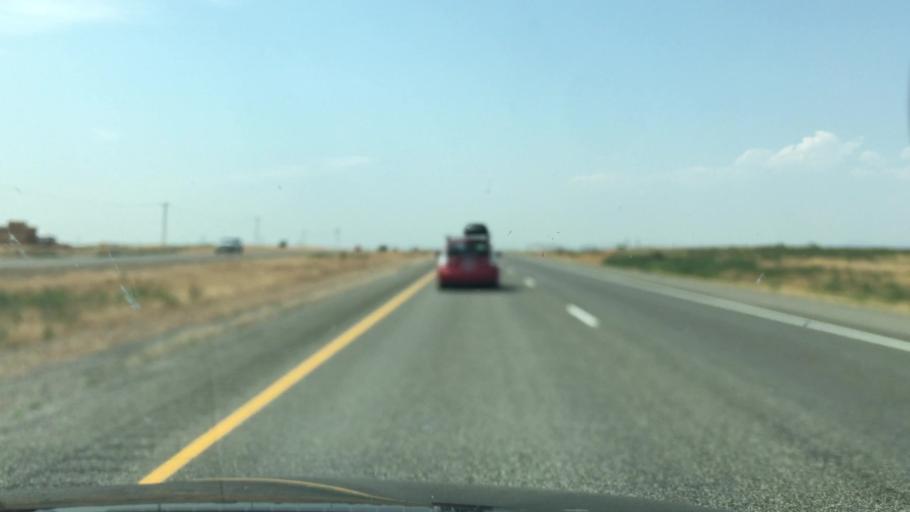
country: US
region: Idaho
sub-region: Gooding County
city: Wendell
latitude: 42.8092
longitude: -114.7722
